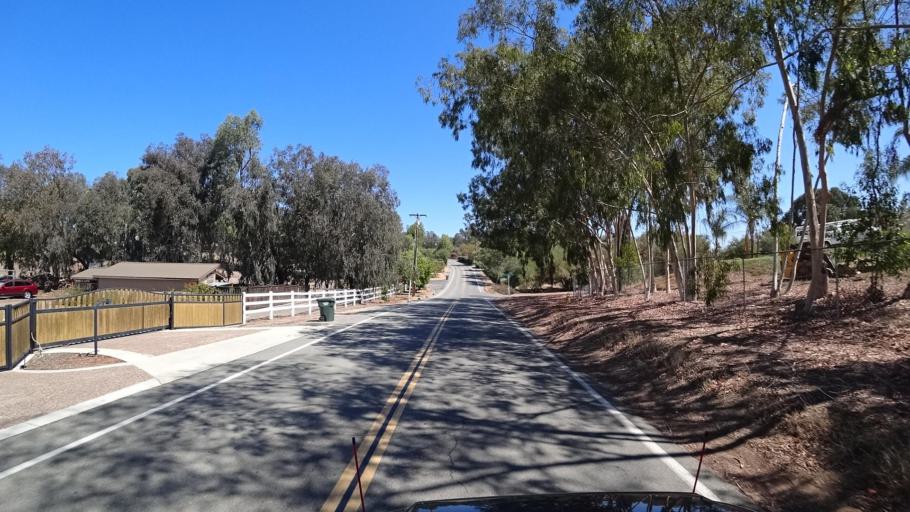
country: US
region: California
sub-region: San Diego County
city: Fallbrook
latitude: 33.3630
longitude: -117.2161
